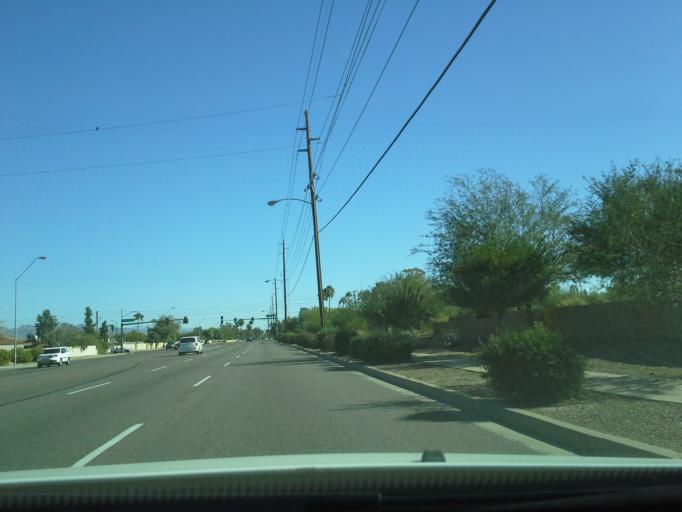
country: US
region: Arizona
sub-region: Maricopa County
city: Paradise Valley
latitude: 33.5826
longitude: -111.9977
